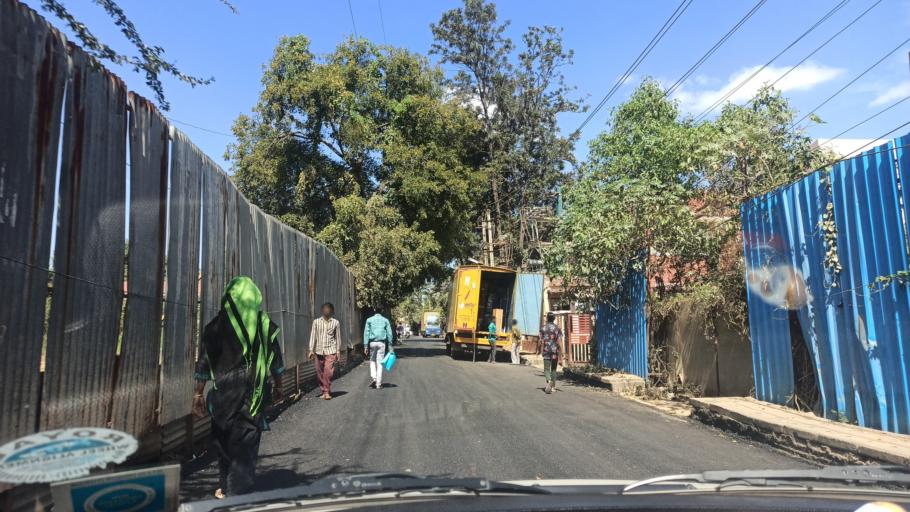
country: IN
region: Karnataka
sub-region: Bangalore Urban
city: Bangalore
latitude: 12.9330
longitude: 77.6861
